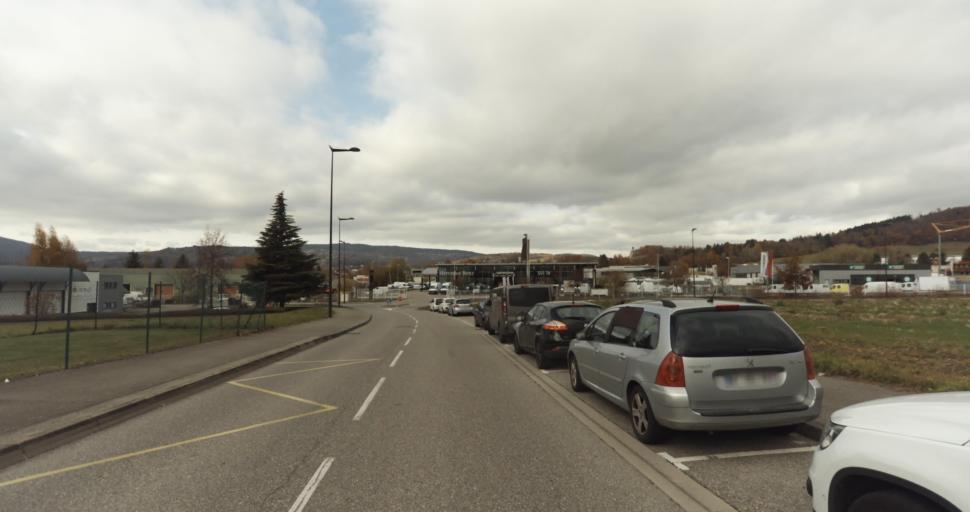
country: FR
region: Rhone-Alpes
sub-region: Departement de la Haute-Savoie
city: Pringy
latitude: 45.9404
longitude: 6.1304
